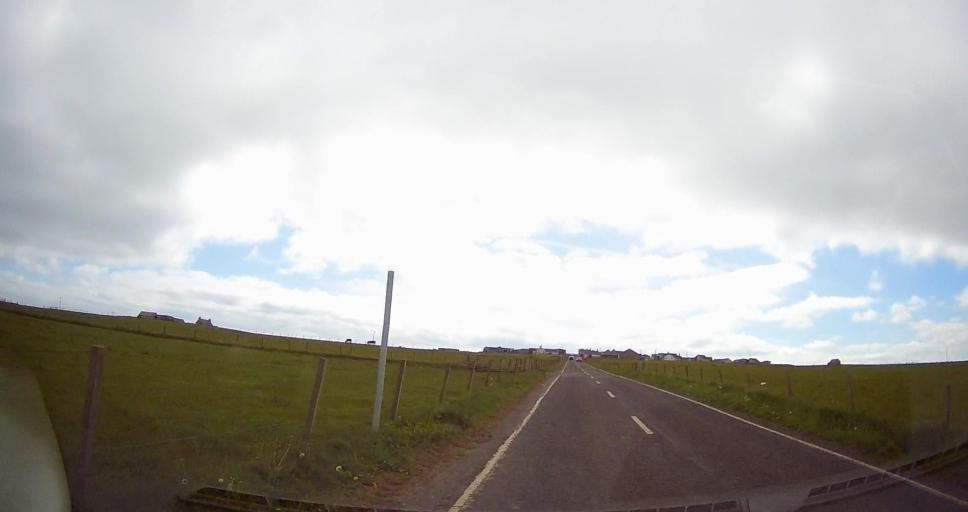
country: GB
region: Scotland
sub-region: Orkney Islands
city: Kirkwall
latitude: 58.9355
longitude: -2.7517
